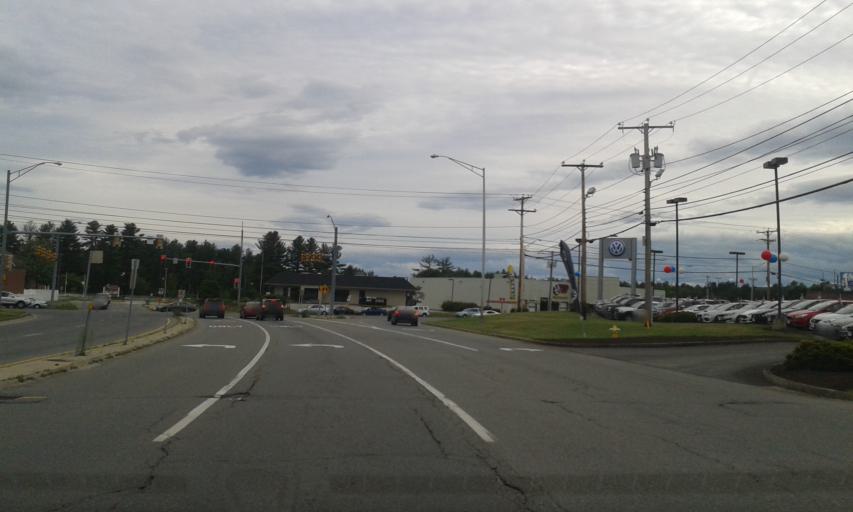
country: US
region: New Hampshire
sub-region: Hillsborough County
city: Litchfield
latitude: 42.8059
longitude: -71.5458
